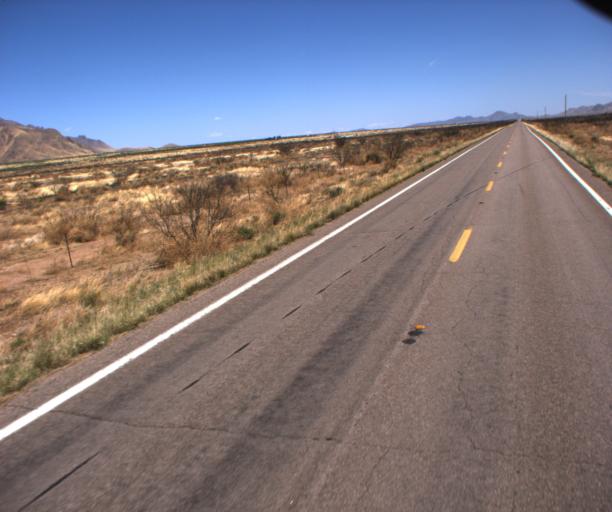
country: US
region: Arizona
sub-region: Cochise County
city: Douglas
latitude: 31.7287
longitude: -109.1063
